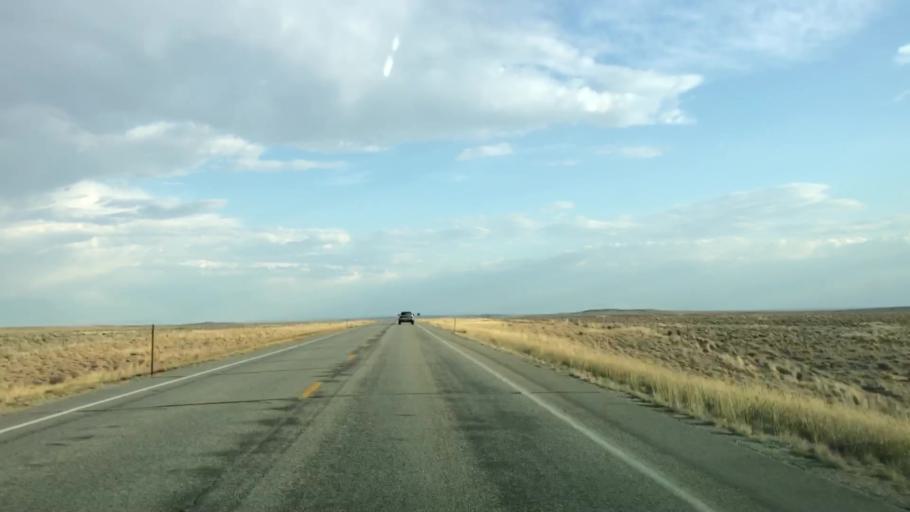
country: US
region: Wyoming
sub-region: Sublette County
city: Pinedale
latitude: 42.3957
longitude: -109.5434
